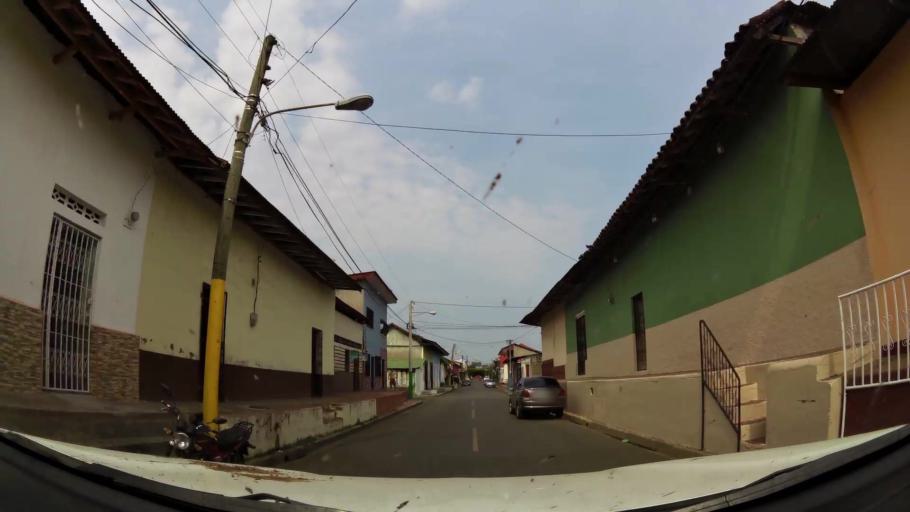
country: NI
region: Masaya
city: Masaya
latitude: 11.9751
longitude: -86.0988
